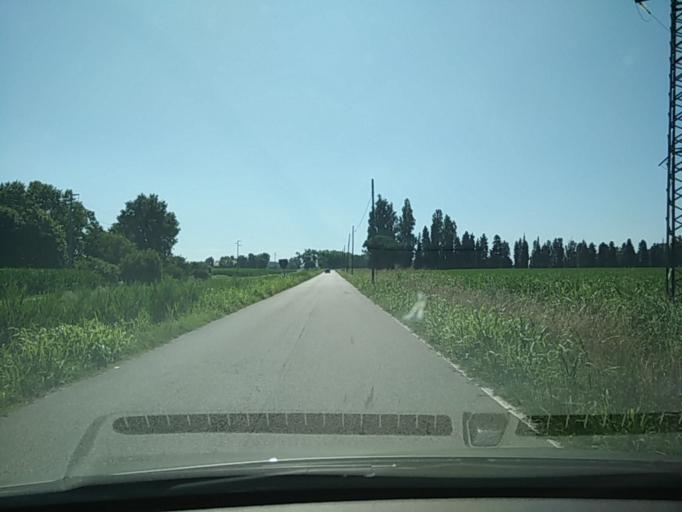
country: IT
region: Veneto
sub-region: Provincia di Venezia
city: San Giorgio di Livenza
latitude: 45.6201
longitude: 12.8011
